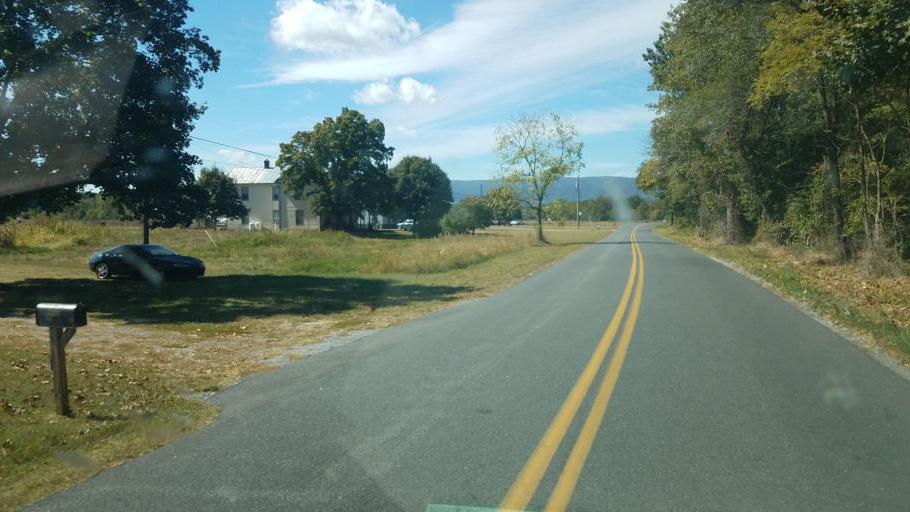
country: US
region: Virginia
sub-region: Page County
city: Shenandoah
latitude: 38.4532
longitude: -78.5770
